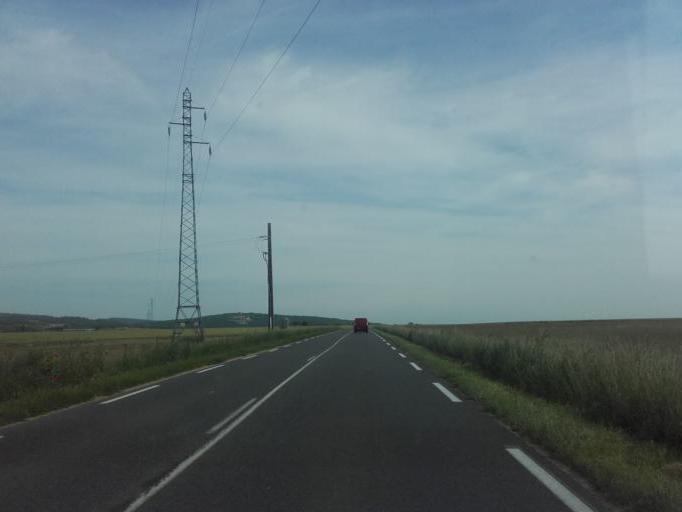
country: FR
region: Bourgogne
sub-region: Departement de Saone-et-Loire
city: Dracy-le-Fort
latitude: 46.8212
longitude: 4.7520
